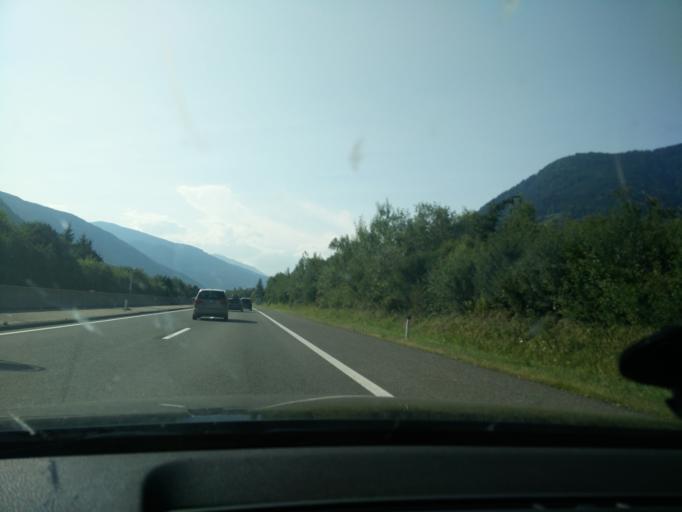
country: AT
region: Carinthia
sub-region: Villach Stadt
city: Villach
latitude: 46.6433
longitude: 13.8852
